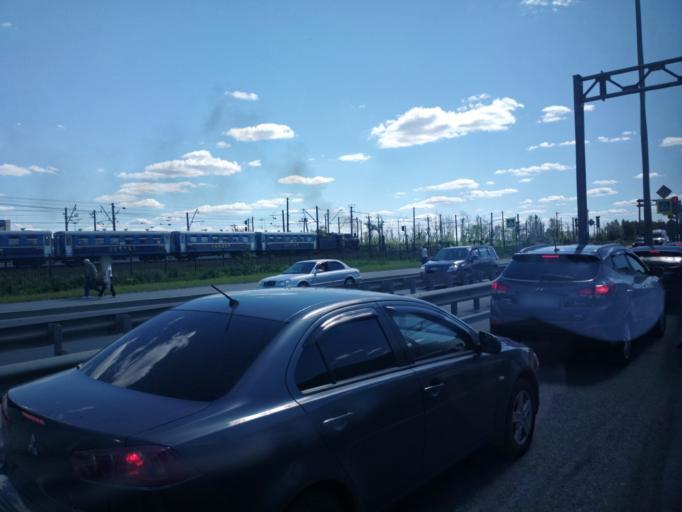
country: RU
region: St.-Petersburg
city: Shushary
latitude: 59.8227
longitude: 30.3788
